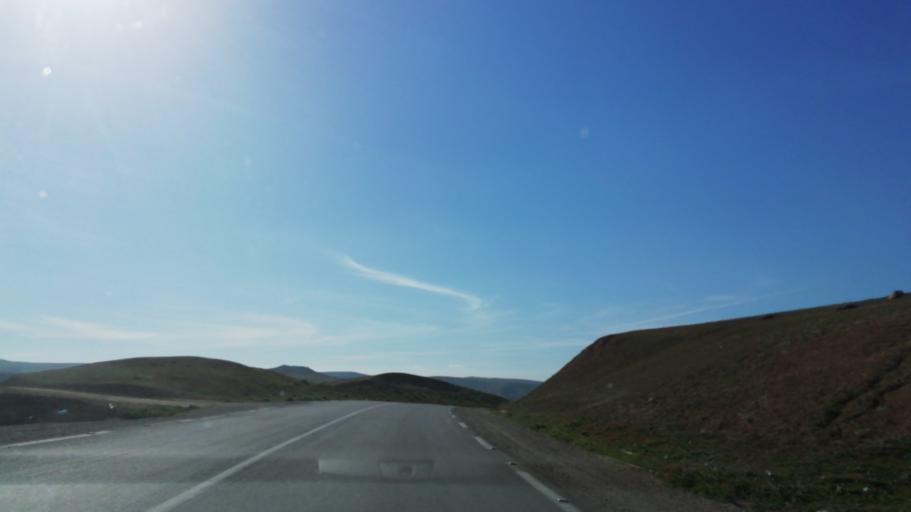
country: DZ
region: Mascara
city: Oued el Abtal
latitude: 35.4491
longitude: 0.8095
